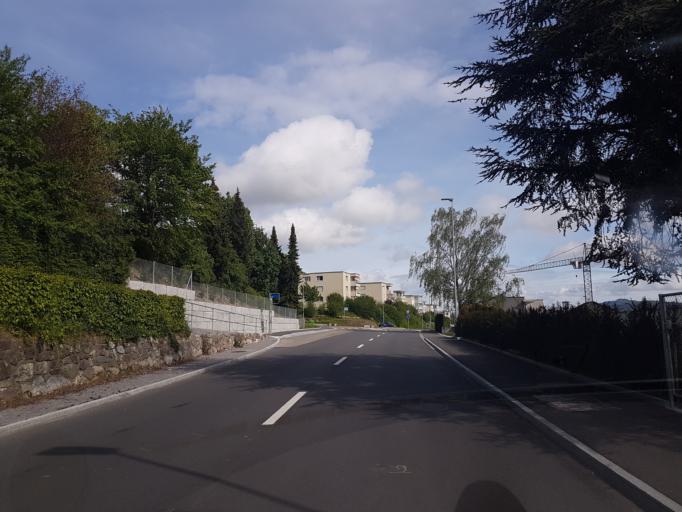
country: CH
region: Zurich
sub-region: Bezirk Dietikon
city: Geroldswil
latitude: 47.4259
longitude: 8.3990
